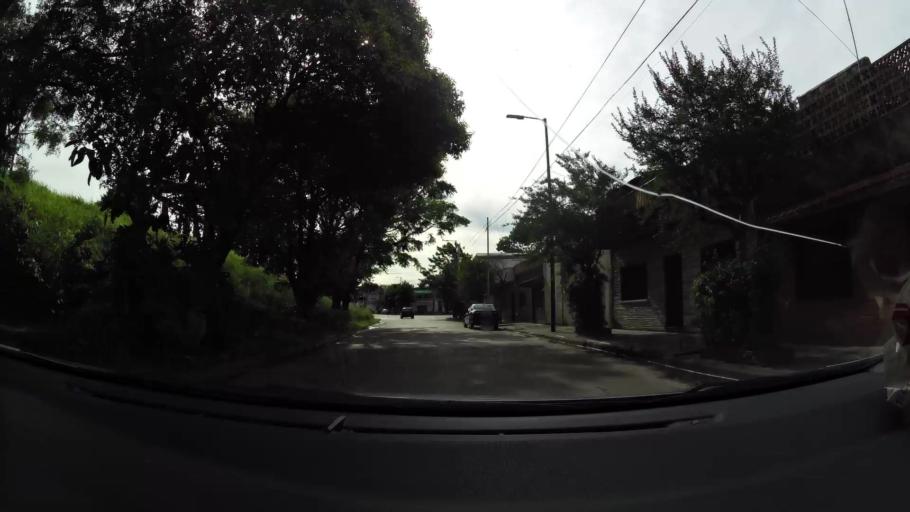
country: AR
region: Buenos Aires F.D.
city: Buenos Aires
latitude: -34.6467
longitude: -58.4240
